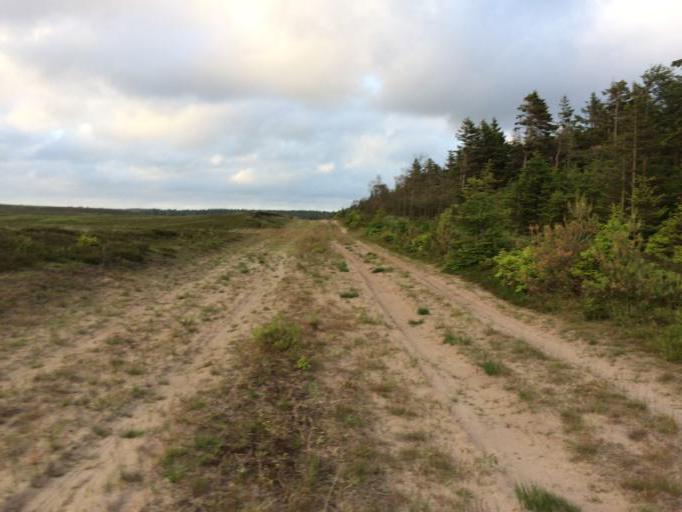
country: DK
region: Central Jutland
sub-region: Holstebro Kommune
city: Ulfborg
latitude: 56.2781
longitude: 8.4539
